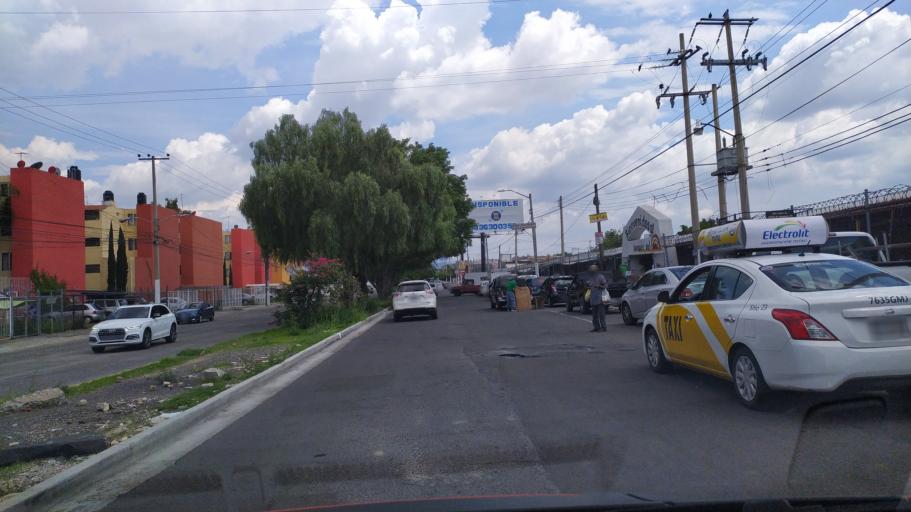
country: MX
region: Jalisco
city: Guadalajara
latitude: 20.6523
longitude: -103.4325
